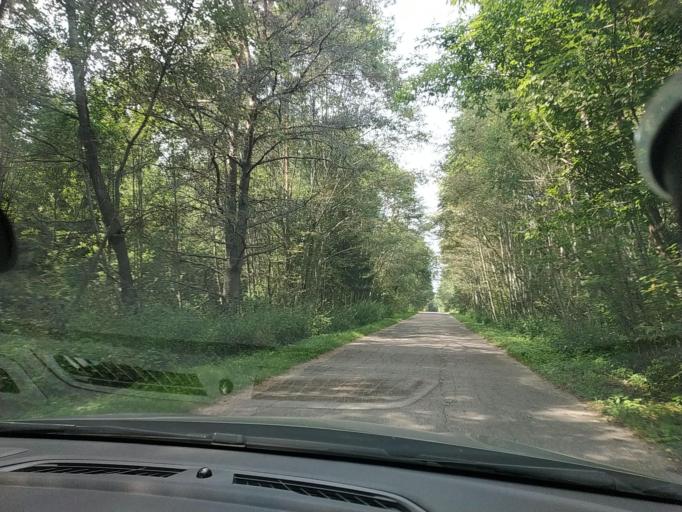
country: LT
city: Nemencine
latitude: 54.8481
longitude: 25.4541
